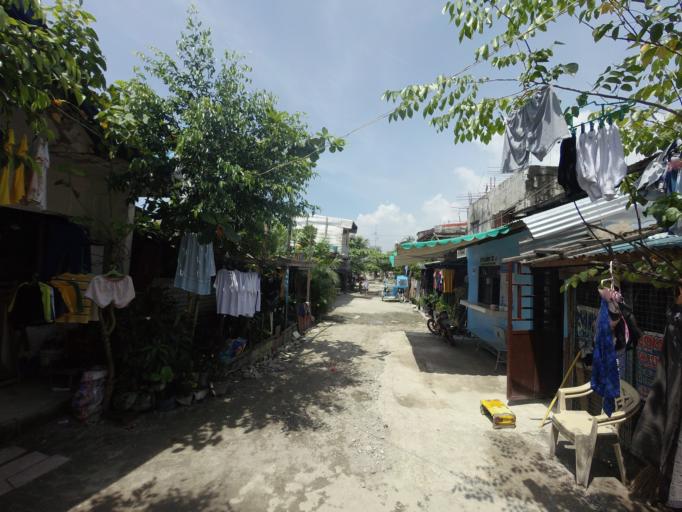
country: PH
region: Calabarzon
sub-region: Province of Rizal
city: Taytay
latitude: 14.5343
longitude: 121.1116
